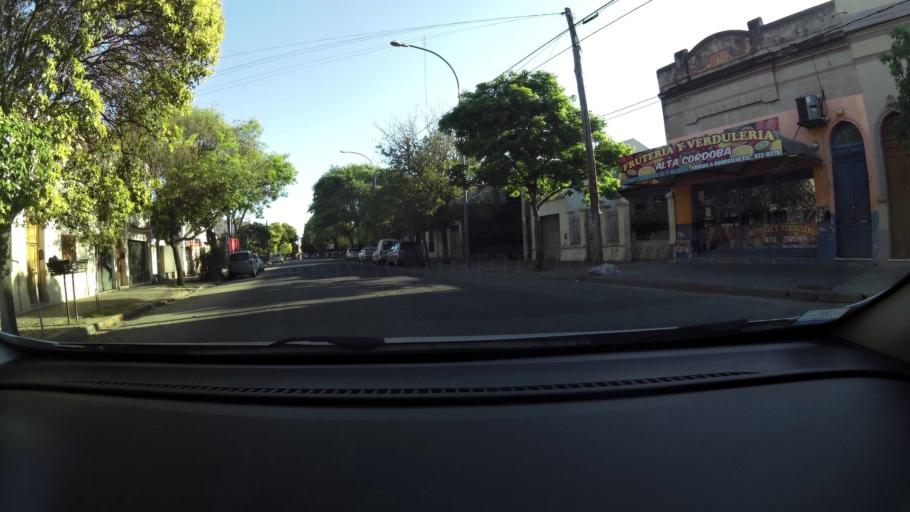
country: AR
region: Cordoba
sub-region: Departamento de Capital
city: Cordoba
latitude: -31.3854
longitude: -64.1838
